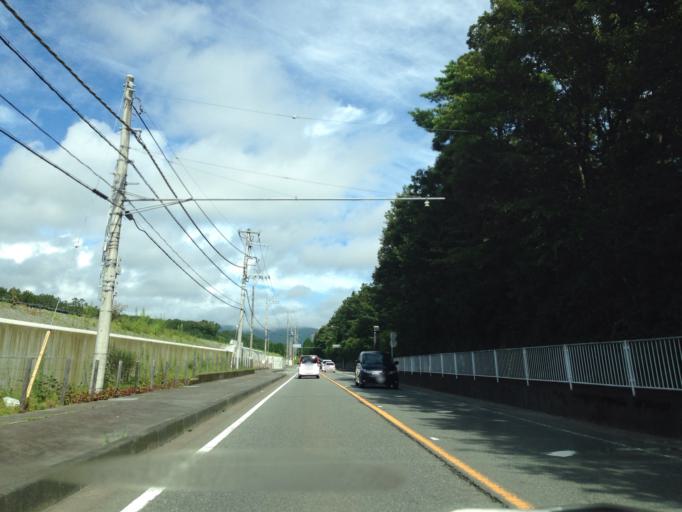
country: JP
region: Shizuoka
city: Gotemba
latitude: 35.3409
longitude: 138.8876
